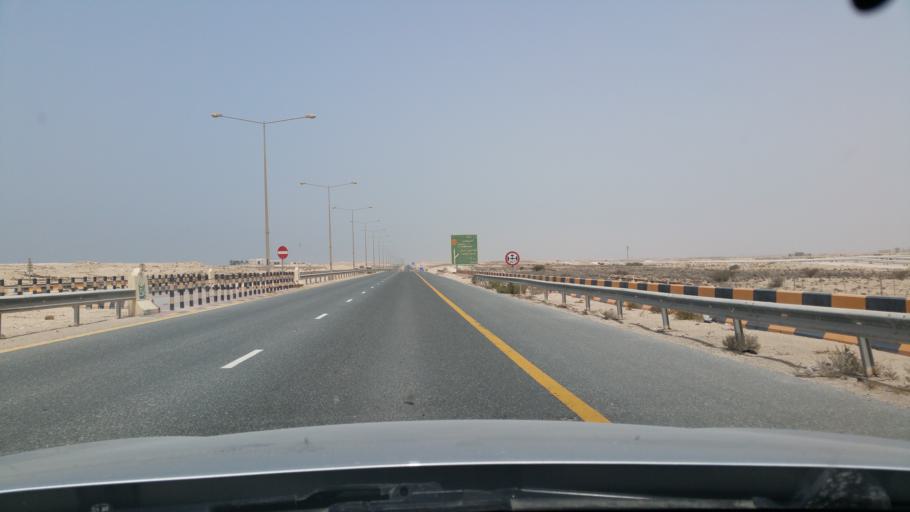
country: QA
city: Umm Bab
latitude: 25.3155
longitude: 50.7911
